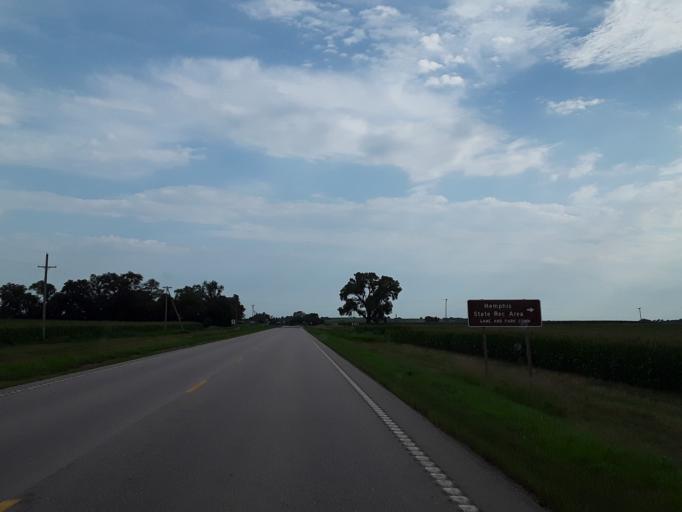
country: US
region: Nebraska
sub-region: Saunders County
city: Ashland
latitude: 41.0986
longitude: -96.4259
